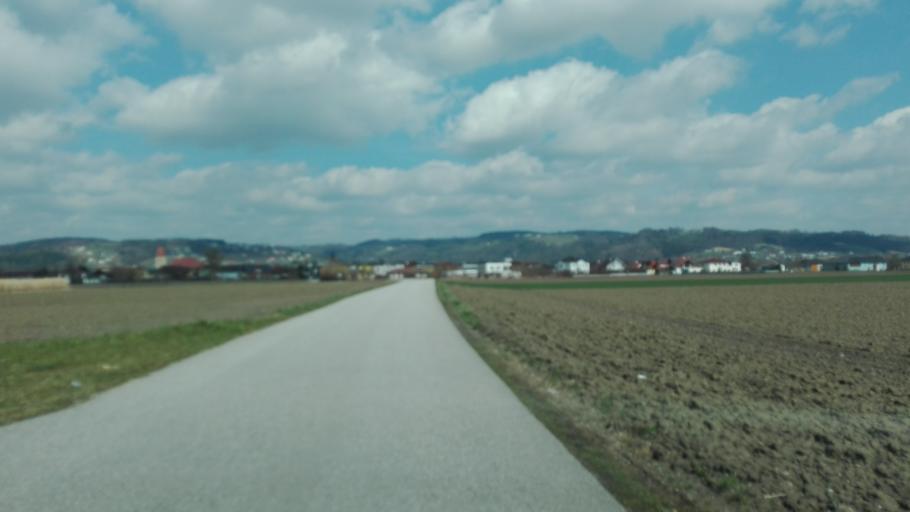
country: AT
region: Upper Austria
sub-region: Politischer Bezirk Urfahr-Umgebung
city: Feldkirchen an der Donau
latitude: 48.3384
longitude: 14.0526
